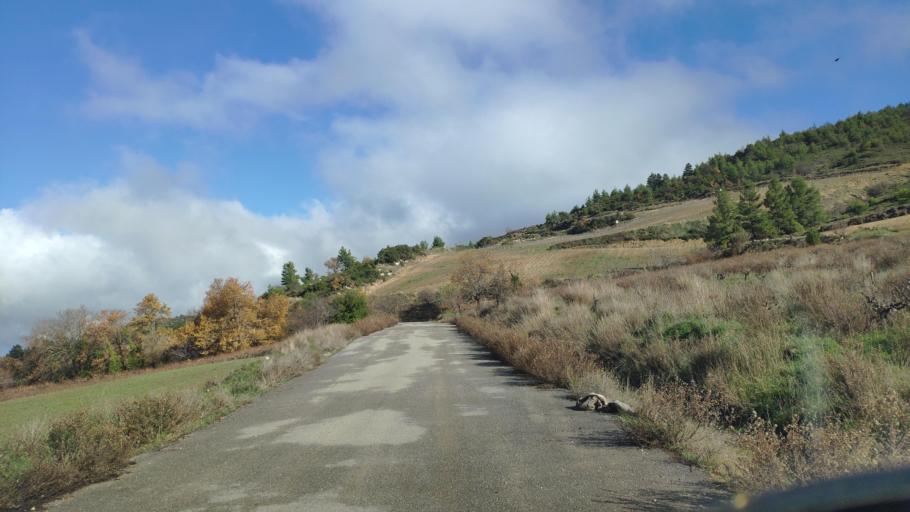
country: GR
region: West Greece
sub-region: Nomos Achaias
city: Aiyira
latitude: 38.0684
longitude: 22.4667
